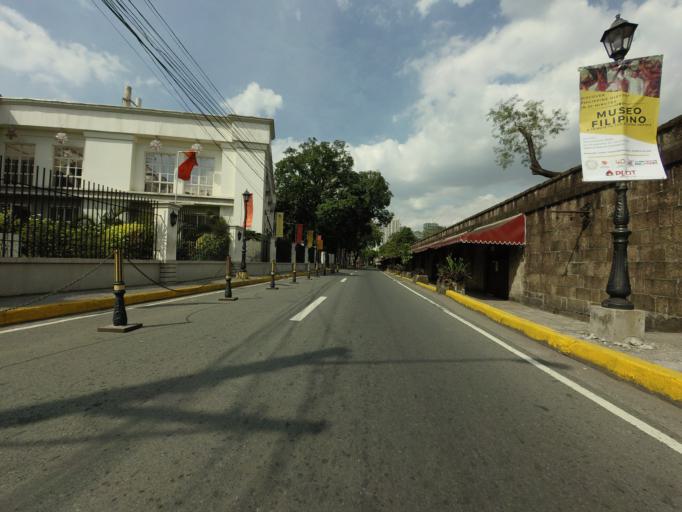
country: PH
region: Metro Manila
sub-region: City of Manila
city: Quiapo
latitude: 14.5907
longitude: 120.9787
